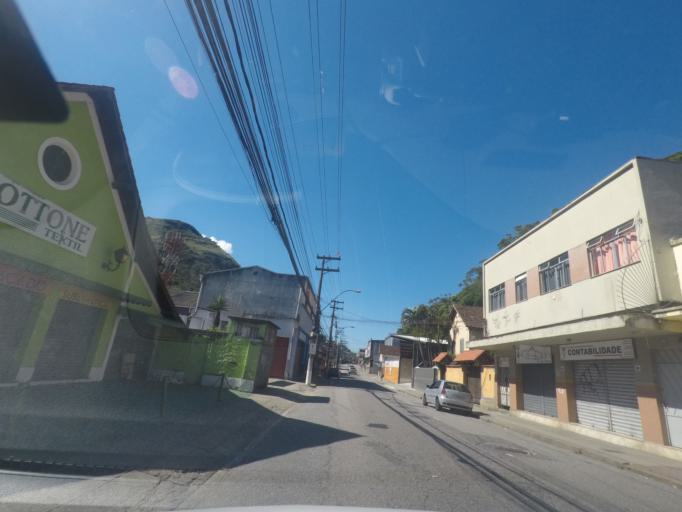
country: BR
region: Rio de Janeiro
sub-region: Petropolis
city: Petropolis
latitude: -22.5196
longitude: -43.1699
